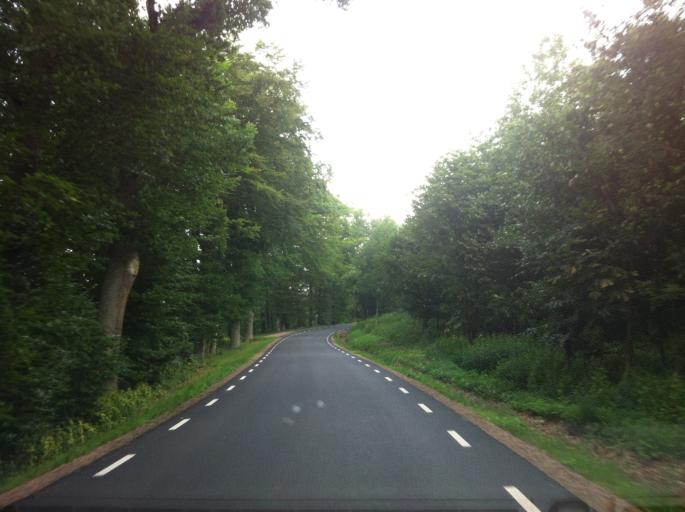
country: SE
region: Skane
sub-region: Trelleborgs Kommun
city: Anderslov
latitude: 55.4746
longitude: 13.3654
